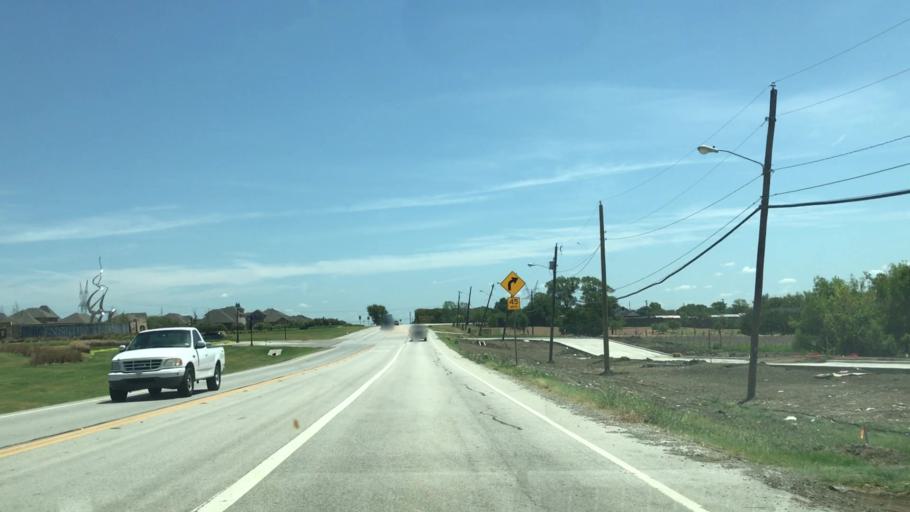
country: US
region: Texas
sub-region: Collin County
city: Saint Paul
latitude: 33.0515
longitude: -96.5549
